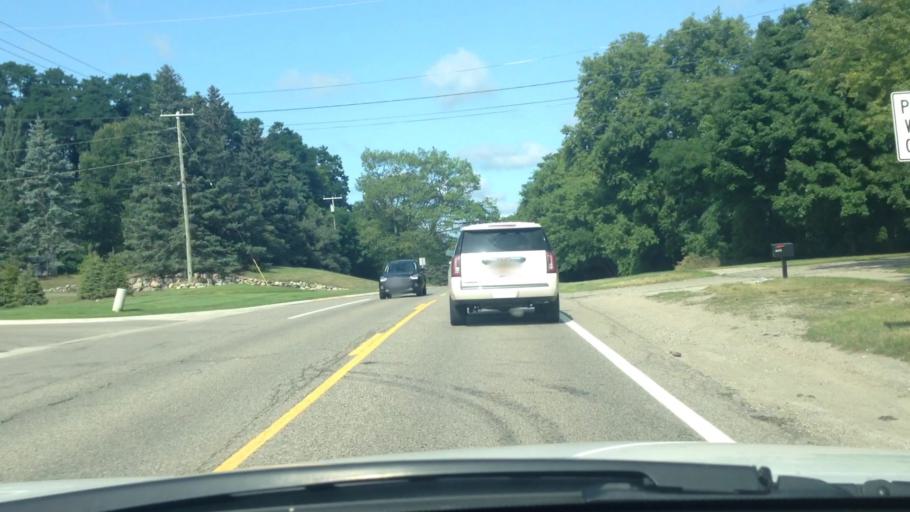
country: US
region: Michigan
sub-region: Oakland County
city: Clarkston
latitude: 42.7516
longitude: -83.3887
